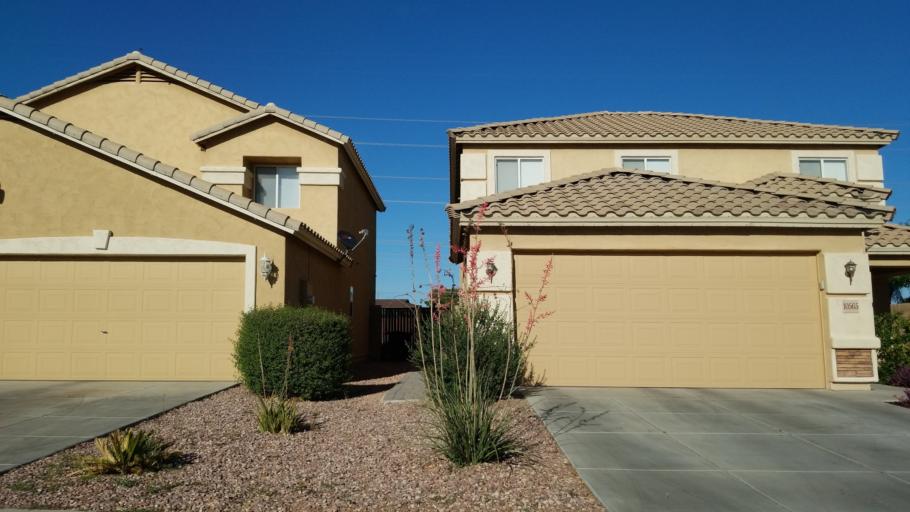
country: US
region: Arizona
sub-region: Maricopa County
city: Youngtown
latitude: 33.5788
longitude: -112.3084
